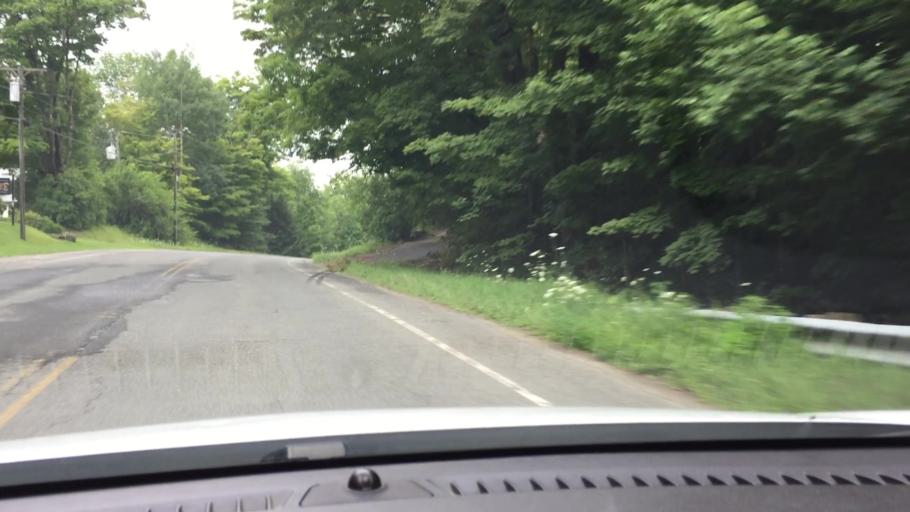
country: US
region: Massachusetts
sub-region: Berkshire County
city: Hinsdale
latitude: 42.4462
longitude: -73.0748
